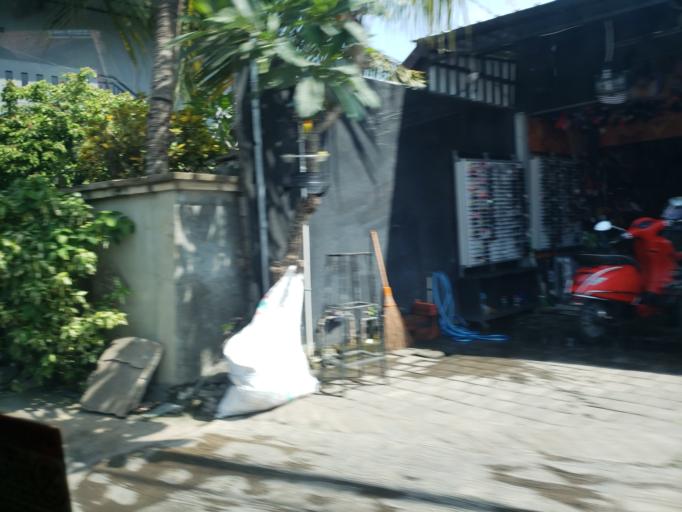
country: ID
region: Bali
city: Jimbaran
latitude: -8.8196
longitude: 115.1527
